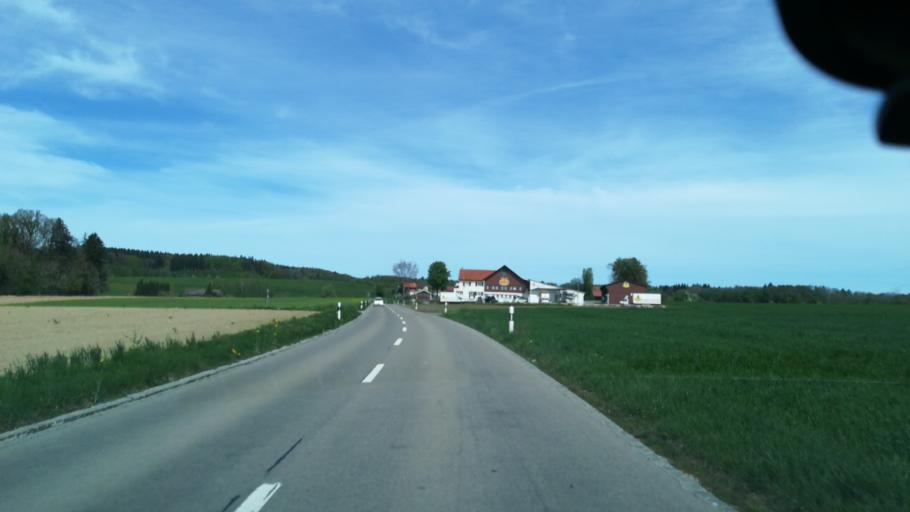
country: CH
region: Thurgau
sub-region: Kreuzlingen District
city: Ermatingen
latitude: 47.6345
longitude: 9.0685
